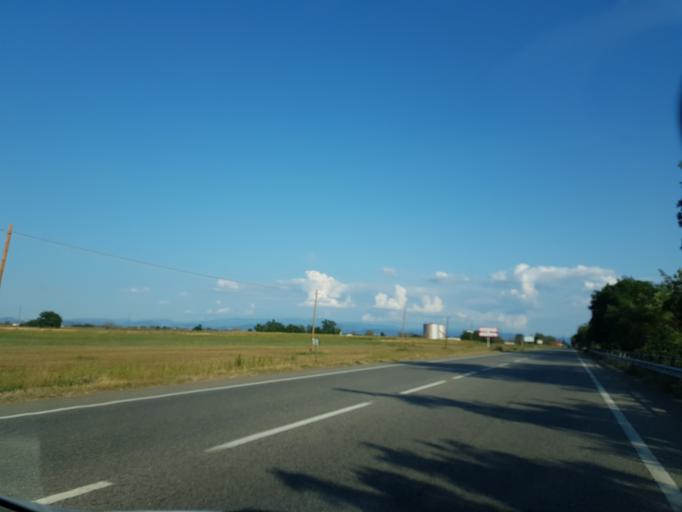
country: IT
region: Piedmont
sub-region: Provincia di Alessandria
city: Litta Parodi-Cascinagrossa
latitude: 44.8636
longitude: 8.7054
